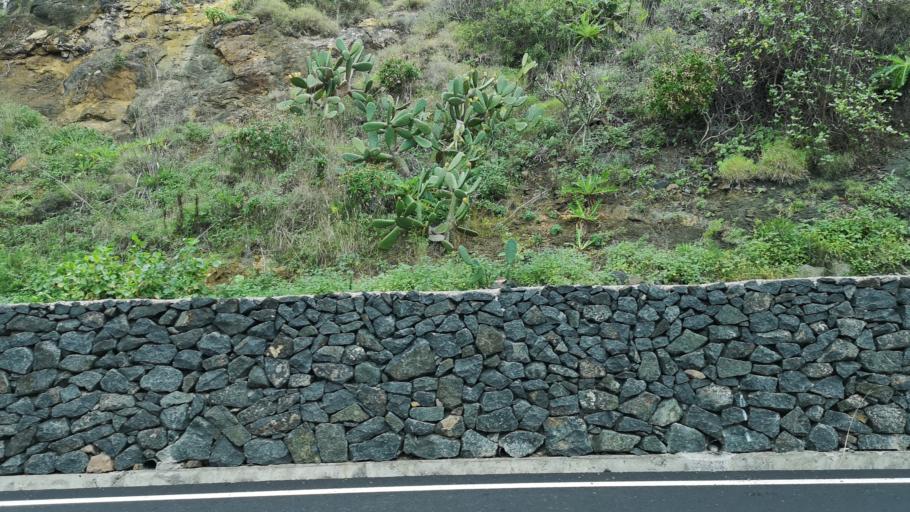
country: ES
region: Canary Islands
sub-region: Provincia de Santa Cruz de Tenerife
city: Agulo
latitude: 28.1872
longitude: -17.2142
